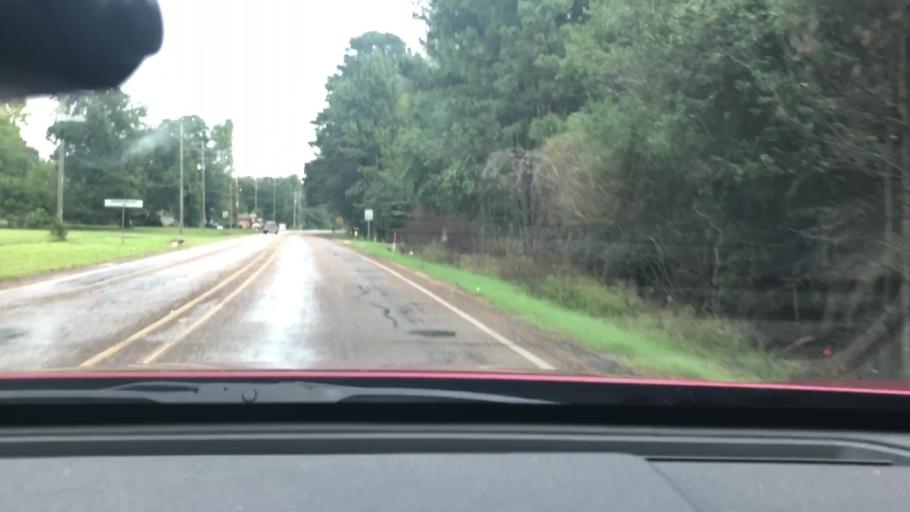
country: US
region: Texas
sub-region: Bowie County
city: Nash
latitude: 33.4421
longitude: -94.1360
